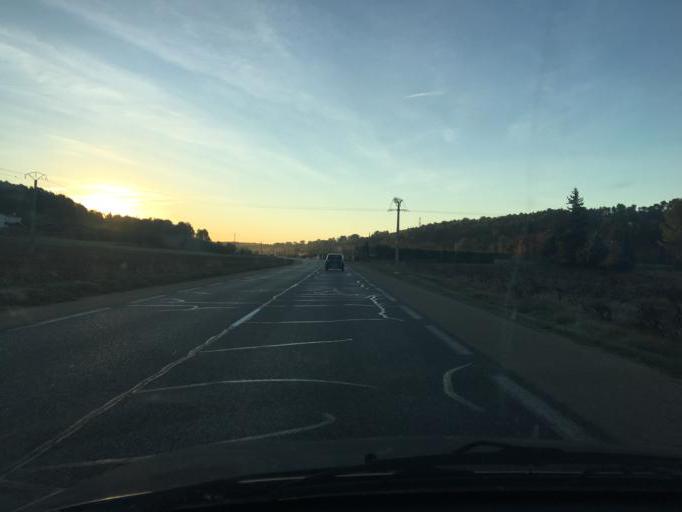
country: FR
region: Provence-Alpes-Cote d'Azur
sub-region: Departement du Var
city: Lorgues
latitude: 43.4763
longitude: 6.3746
